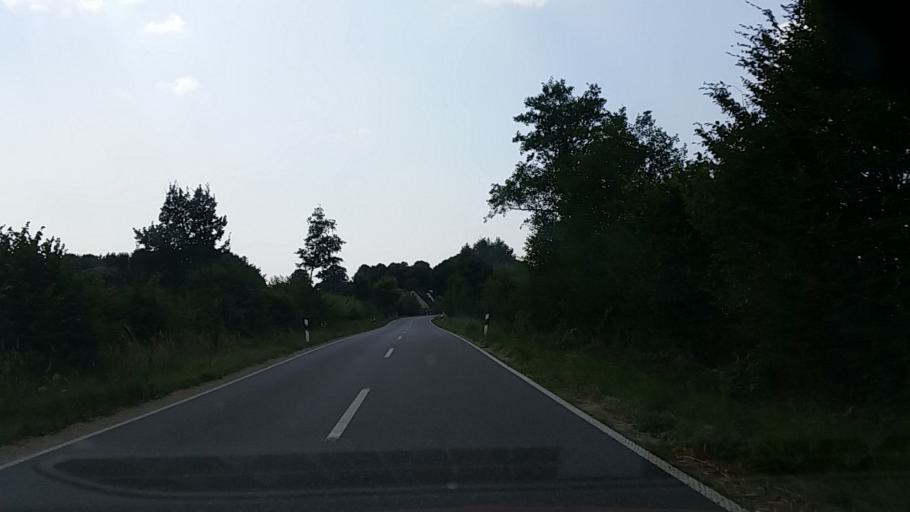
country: DE
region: Schleswig-Holstein
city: Balau
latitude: 53.6179
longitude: 10.6278
